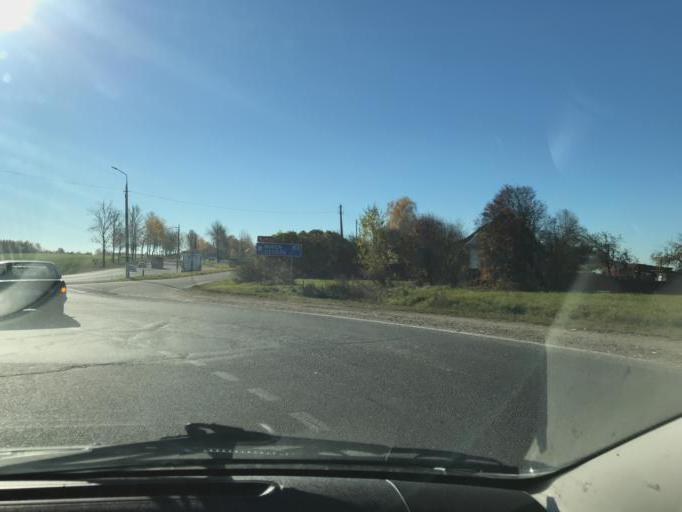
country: BY
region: Vitebsk
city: Lyepyel'
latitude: 54.9175
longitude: 28.7354
